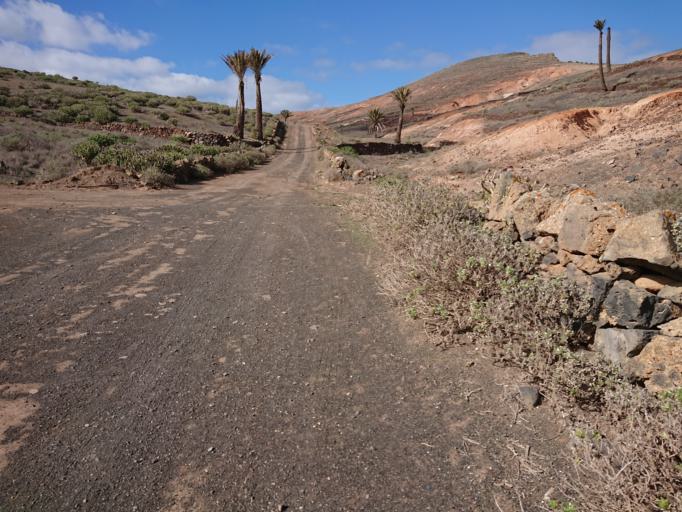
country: ES
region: Canary Islands
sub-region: Provincia de Las Palmas
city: Haria
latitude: 29.1449
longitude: -13.5116
